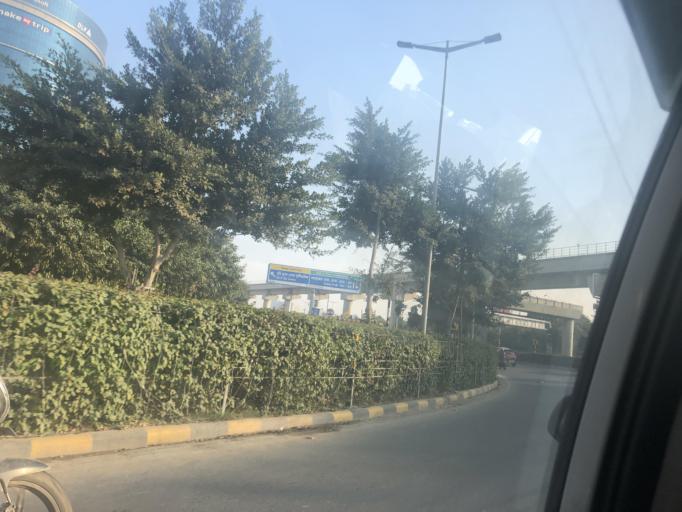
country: IN
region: Haryana
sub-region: Gurgaon
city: Gurgaon
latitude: 28.4899
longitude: 77.0901
